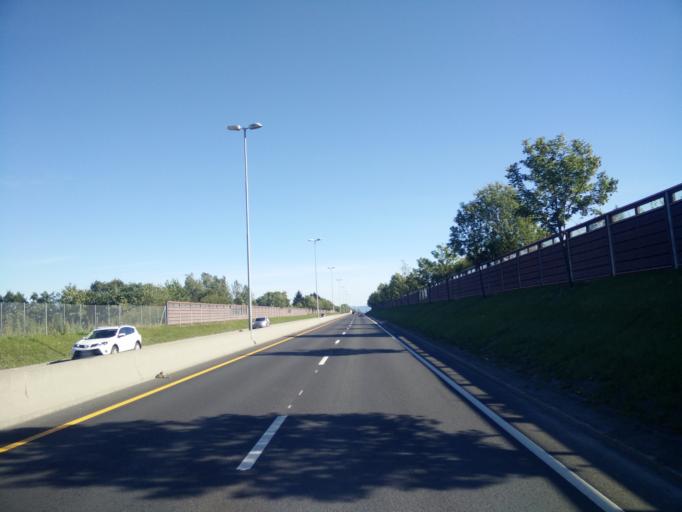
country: NO
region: Sor-Trondelag
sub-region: Trondheim
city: Trondheim
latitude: 63.4120
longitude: 10.4469
